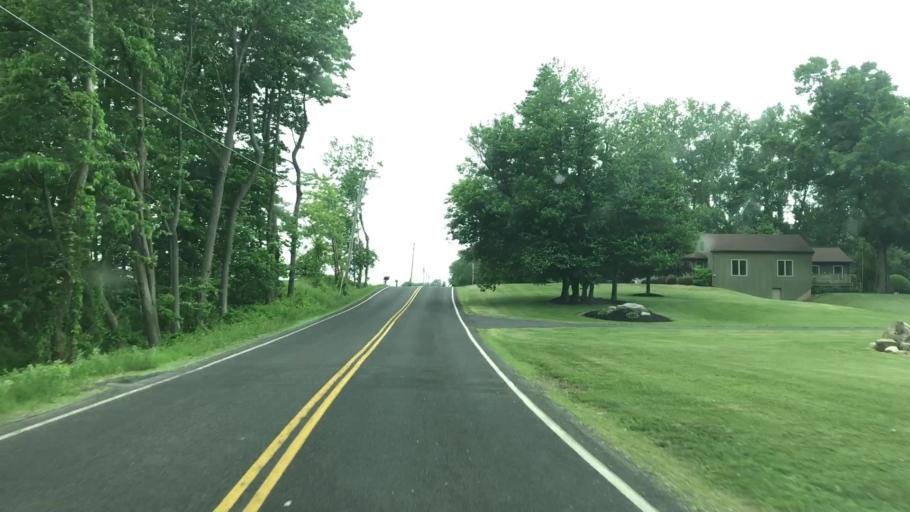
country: US
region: New York
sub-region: Wayne County
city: Macedon
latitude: 43.1163
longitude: -77.2996
